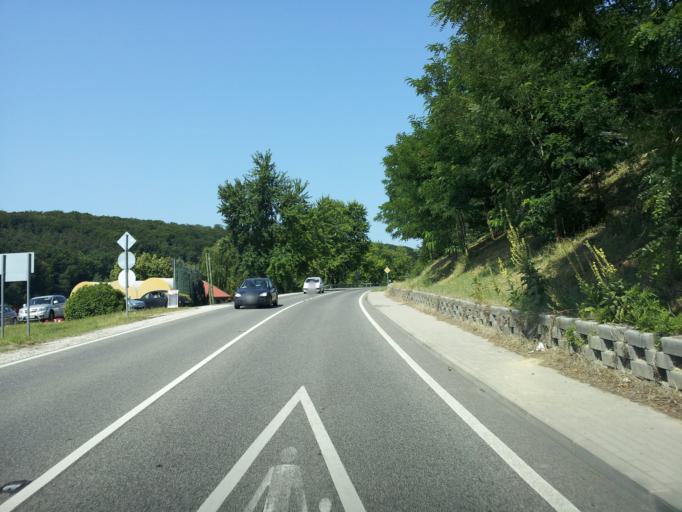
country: HU
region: Zala
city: Heviz
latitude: 46.8051
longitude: 17.0925
